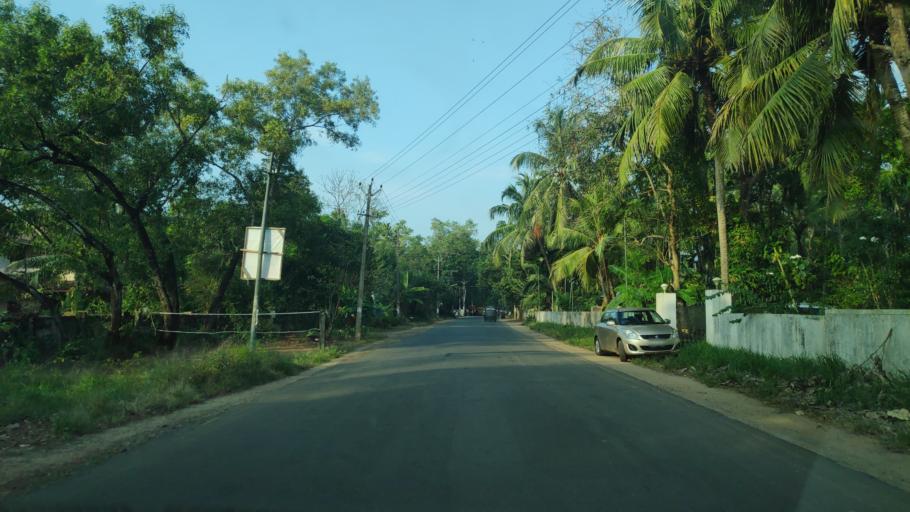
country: IN
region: Kerala
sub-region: Alappuzha
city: Shertallai
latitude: 9.6120
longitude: 76.3622
